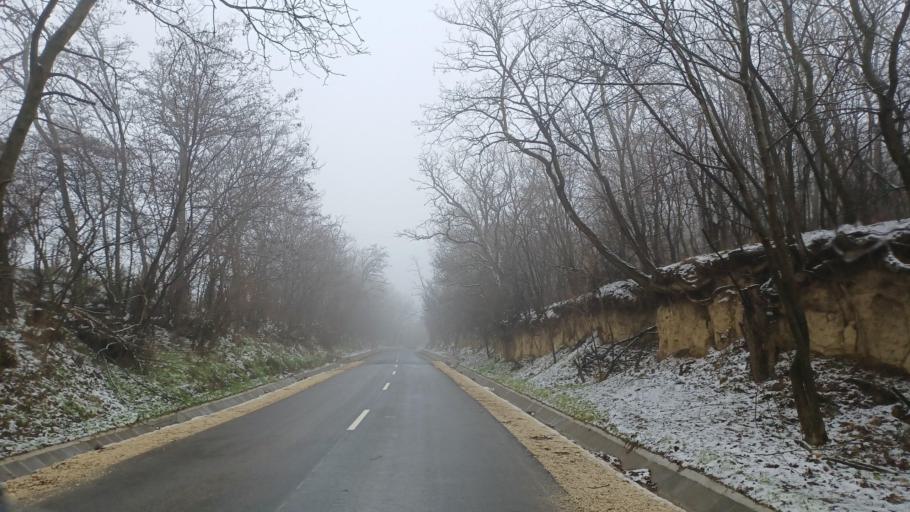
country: HU
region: Tolna
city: Gyonk
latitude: 46.5747
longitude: 18.4743
